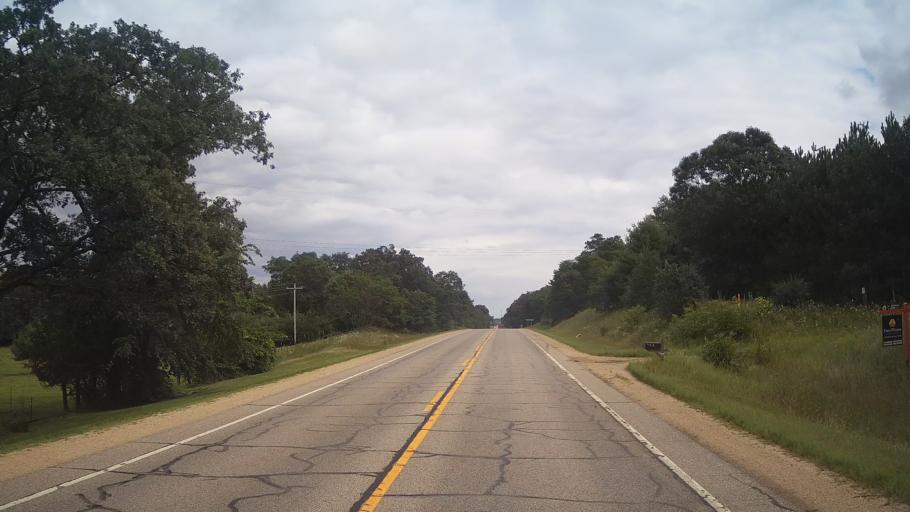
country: US
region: Wisconsin
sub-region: Waushara County
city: Wautoma
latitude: 44.0684
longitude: -89.3199
